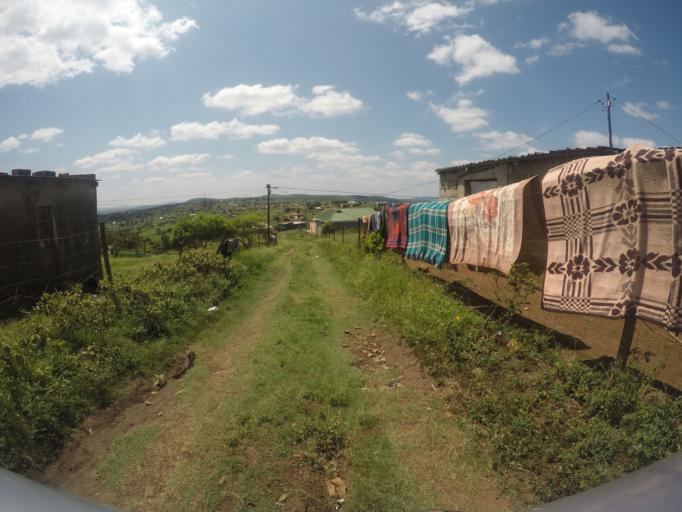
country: ZA
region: KwaZulu-Natal
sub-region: uThungulu District Municipality
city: Empangeni
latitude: -28.6094
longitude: 31.7325
